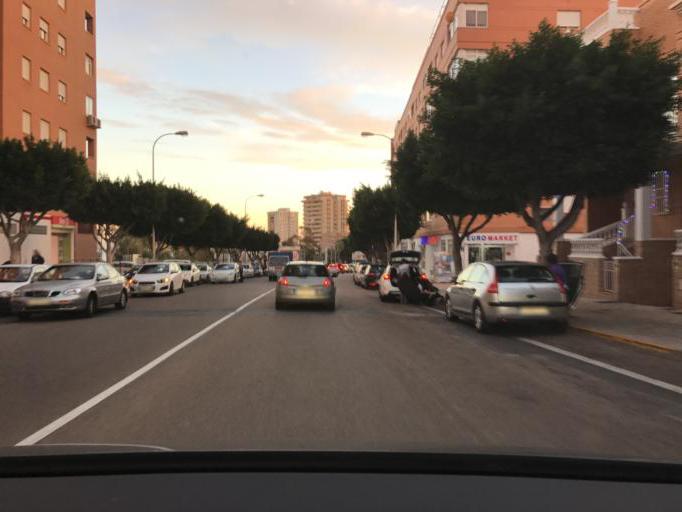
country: ES
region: Andalusia
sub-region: Provincia de Almeria
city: Aguadulce
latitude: 36.8141
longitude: -2.5791
